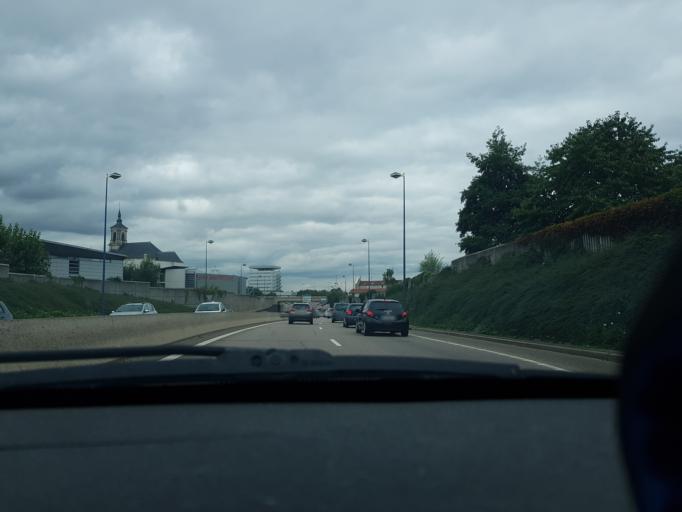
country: FR
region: Lorraine
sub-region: Departement de Meurthe-et-Moselle
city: Jarville-la-Malgrange
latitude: 48.6745
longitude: 6.1971
